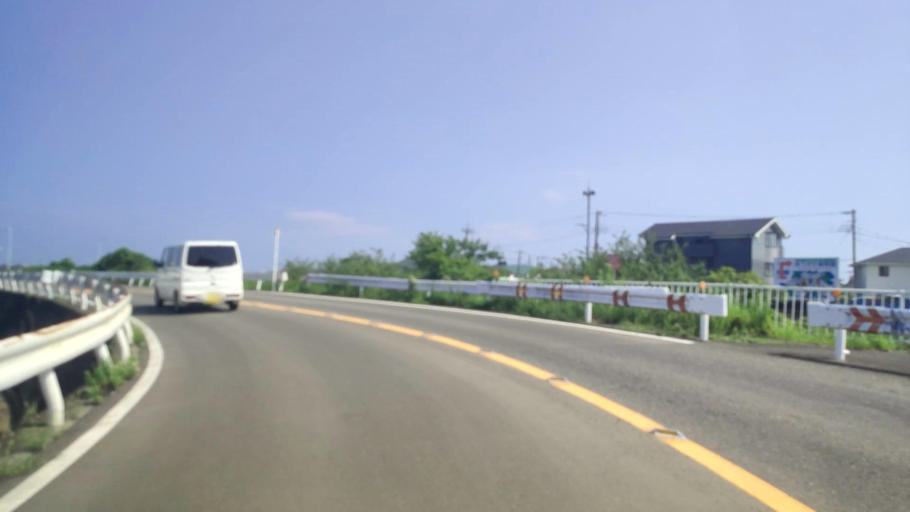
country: JP
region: Kanagawa
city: Isehara
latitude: 35.3680
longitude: 139.3155
